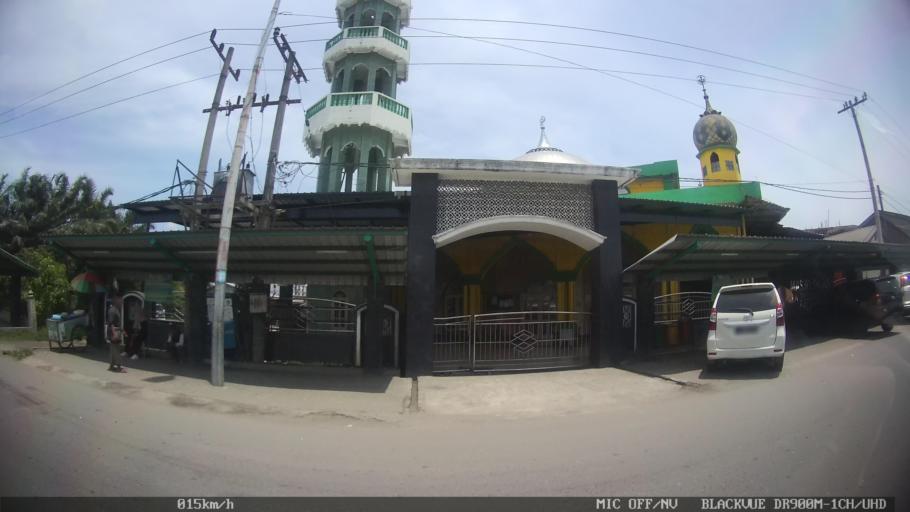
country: ID
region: North Sumatra
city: Belawan
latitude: 3.7715
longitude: 98.6819
